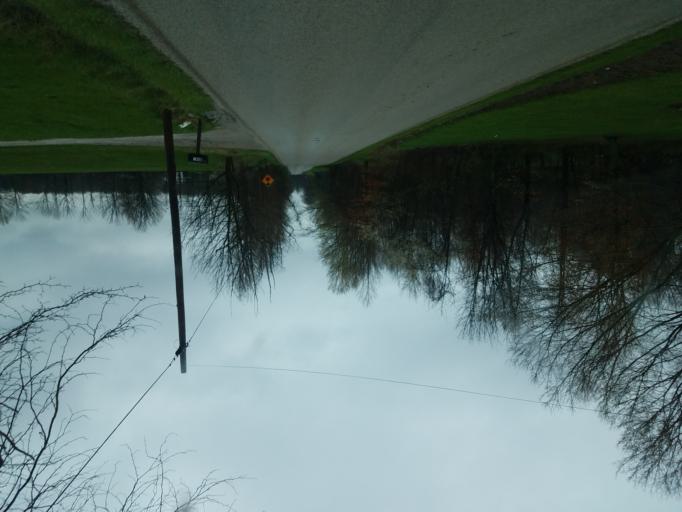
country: US
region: Ohio
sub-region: Morrow County
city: Mount Gilead
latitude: 40.4584
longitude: -82.8069
